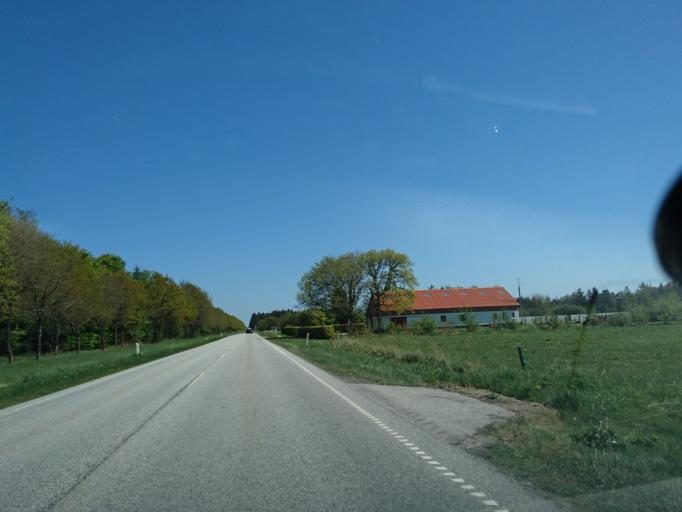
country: DK
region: North Denmark
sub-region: Hjorring Kommune
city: Sindal
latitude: 57.5873
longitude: 10.2427
